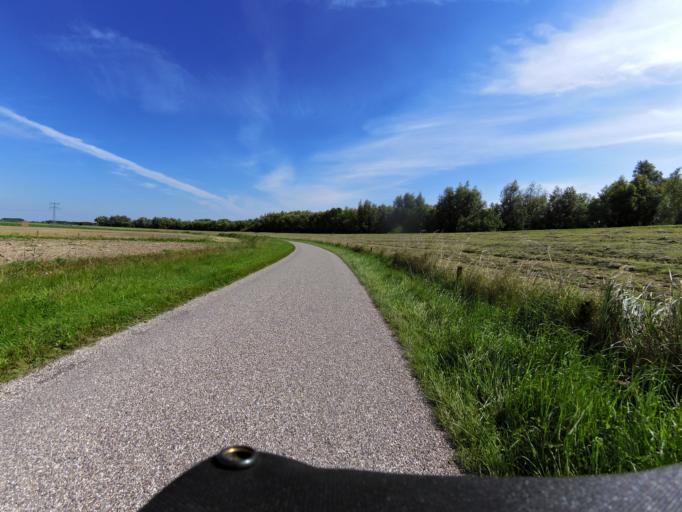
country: NL
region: North Brabant
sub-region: Gemeente Geertruidenberg
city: Geertruidenberg
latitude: 51.7604
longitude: 4.8425
